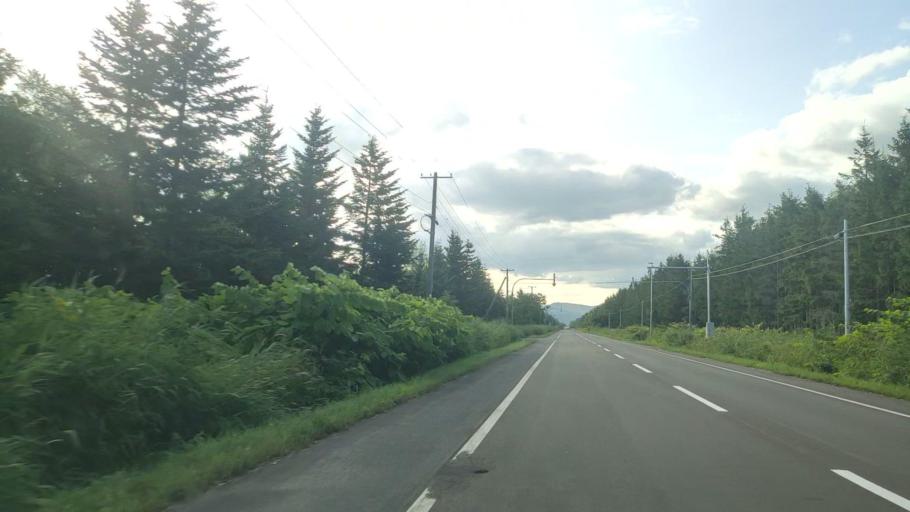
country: JP
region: Hokkaido
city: Makubetsu
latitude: 44.8846
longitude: 142.0130
